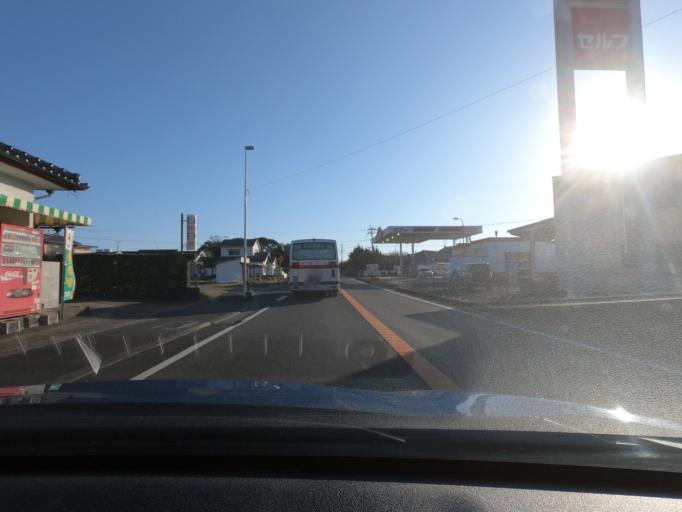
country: JP
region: Kagoshima
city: Akune
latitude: 31.9820
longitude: 130.2036
